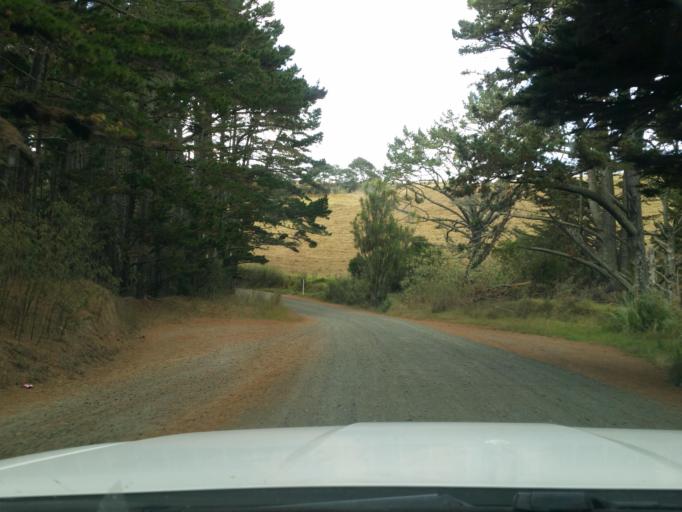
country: NZ
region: Auckland
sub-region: Auckland
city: Wellsford
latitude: -36.3126
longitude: 174.1290
